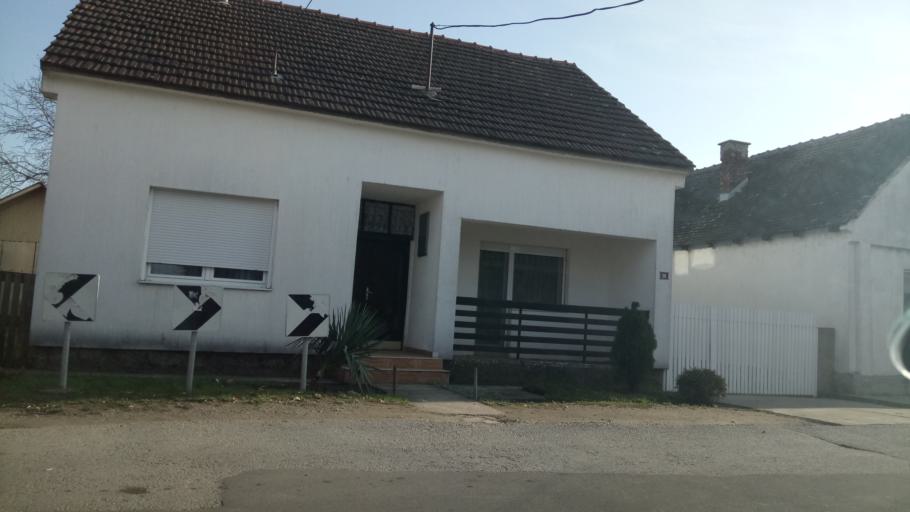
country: RS
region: Autonomna Pokrajina Vojvodina
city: Nova Pazova
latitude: 44.9490
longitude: 20.2211
